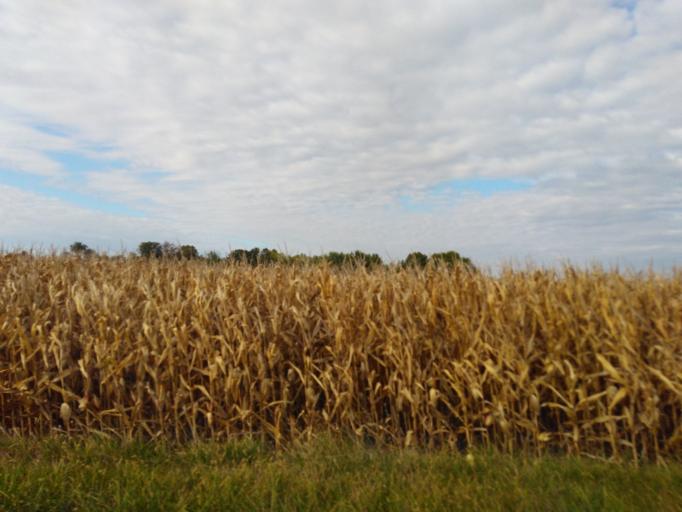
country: US
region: Illinois
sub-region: Bond County
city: Greenville
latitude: 38.9019
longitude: -89.3901
